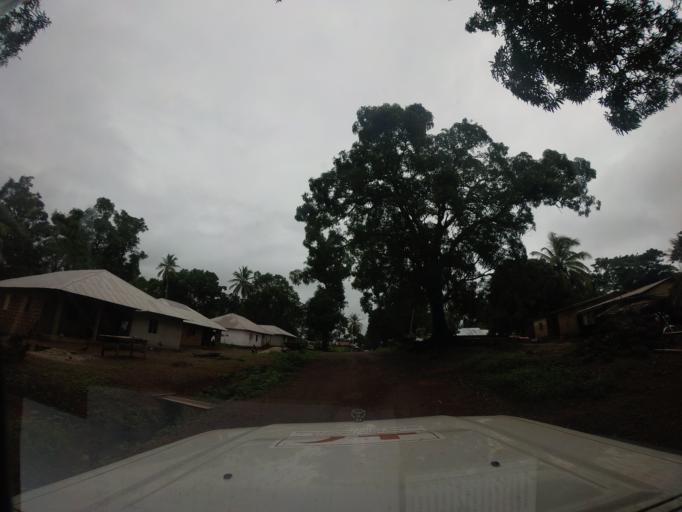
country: SL
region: Northern Province
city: Kambia
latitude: 9.1651
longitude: -12.8782
